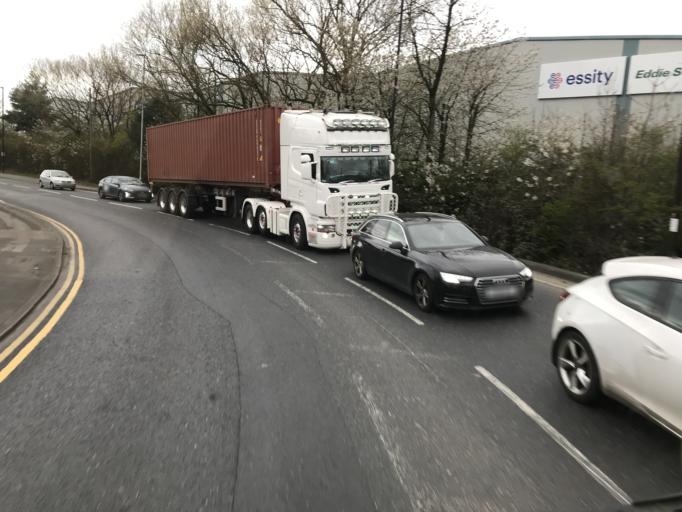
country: GB
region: England
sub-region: City and Borough of Salford
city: Eccles
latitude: 53.4736
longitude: -2.3355
